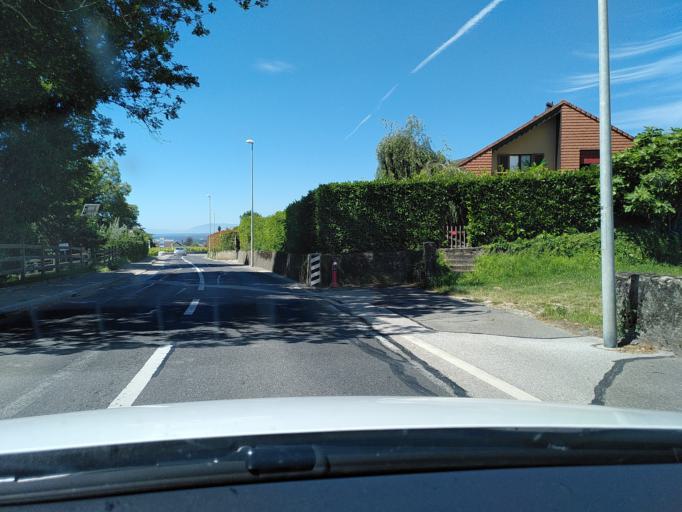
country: CH
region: Vaud
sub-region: Morges District
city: Aubonne
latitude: 46.4904
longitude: 6.3859
